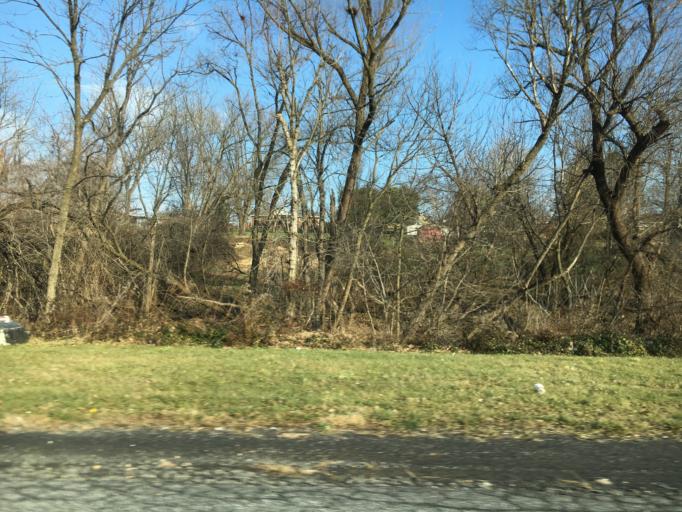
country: US
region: Pennsylvania
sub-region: Lehigh County
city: Stiles
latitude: 40.6637
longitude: -75.5108
